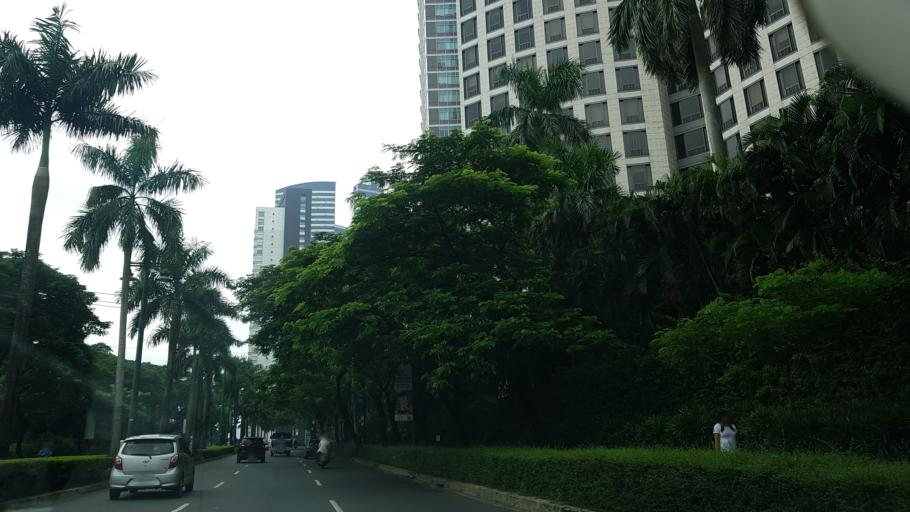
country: PH
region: Metro Manila
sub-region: Makati City
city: Makati City
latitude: 14.5429
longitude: 121.0464
